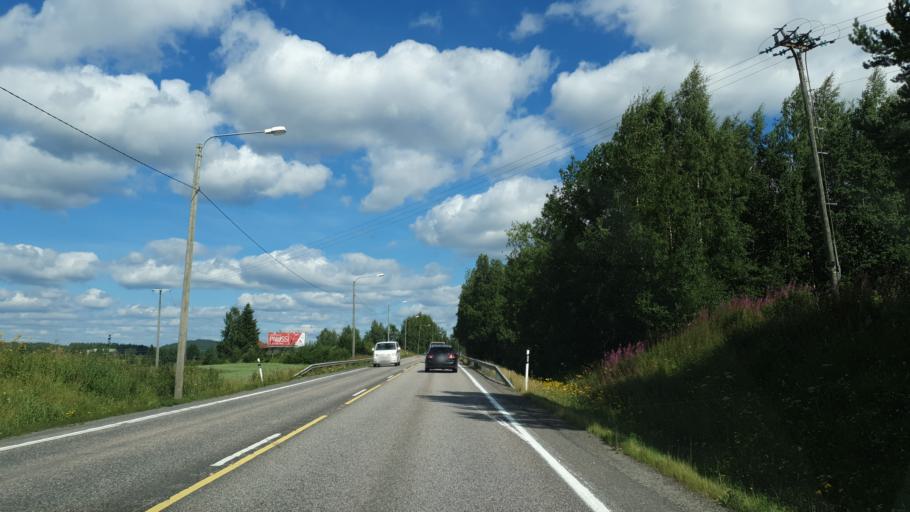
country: FI
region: Central Finland
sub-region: Jaemsae
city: Jaemsae
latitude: 61.8481
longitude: 25.1545
